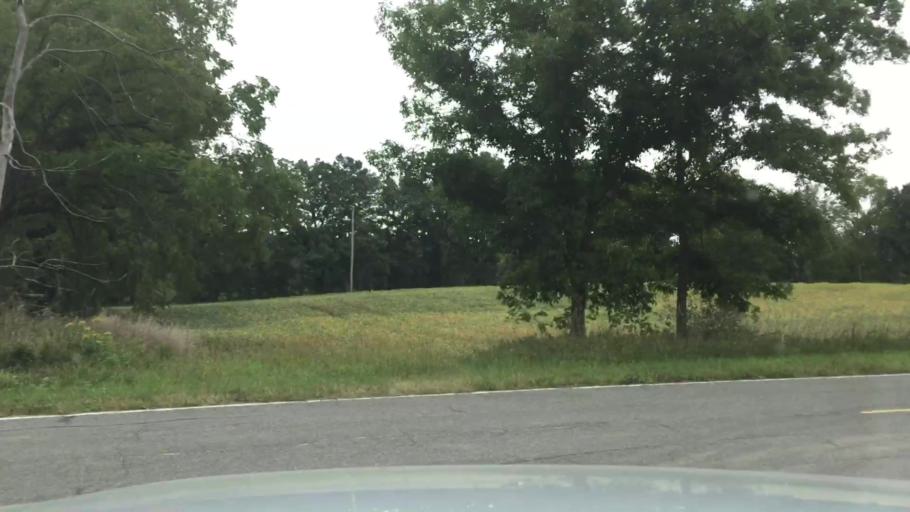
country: US
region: Michigan
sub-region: Shiawassee County
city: Corunna
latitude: 42.9361
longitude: -84.1048
